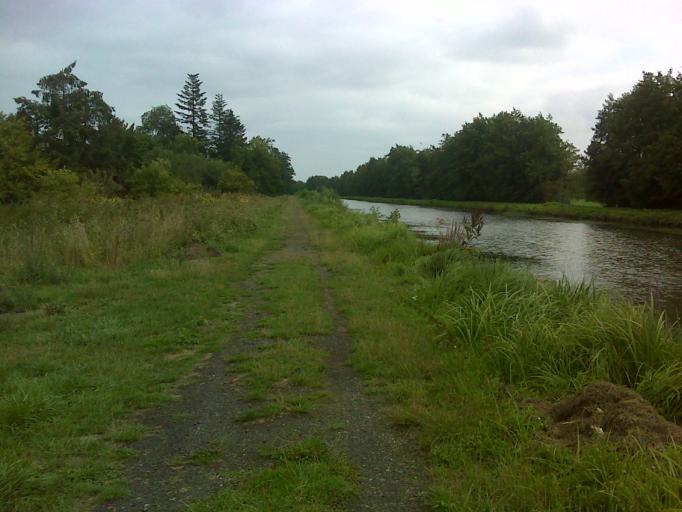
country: FR
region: Nord-Pas-de-Calais
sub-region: Departement du Nord
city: Bousies
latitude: 50.1027
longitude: 3.6392
